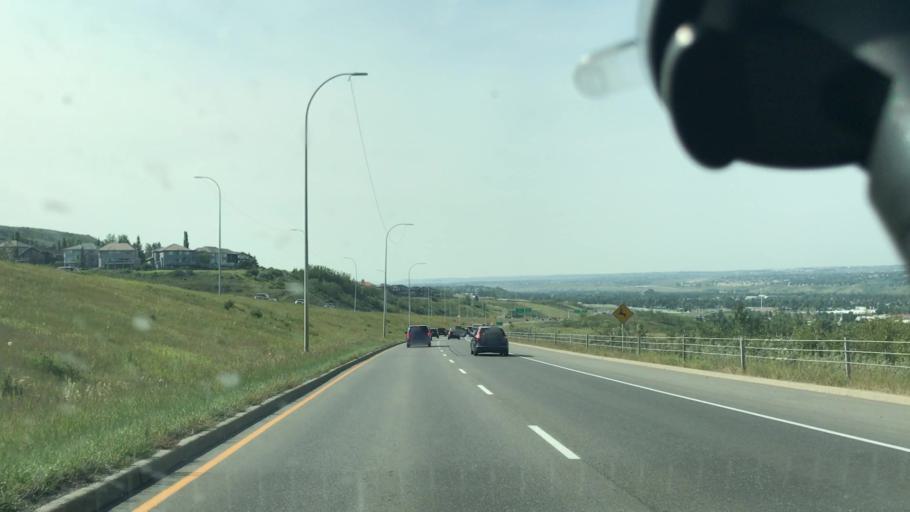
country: CA
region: Alberta
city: Calgary
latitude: 51.0687
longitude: -114.1776
